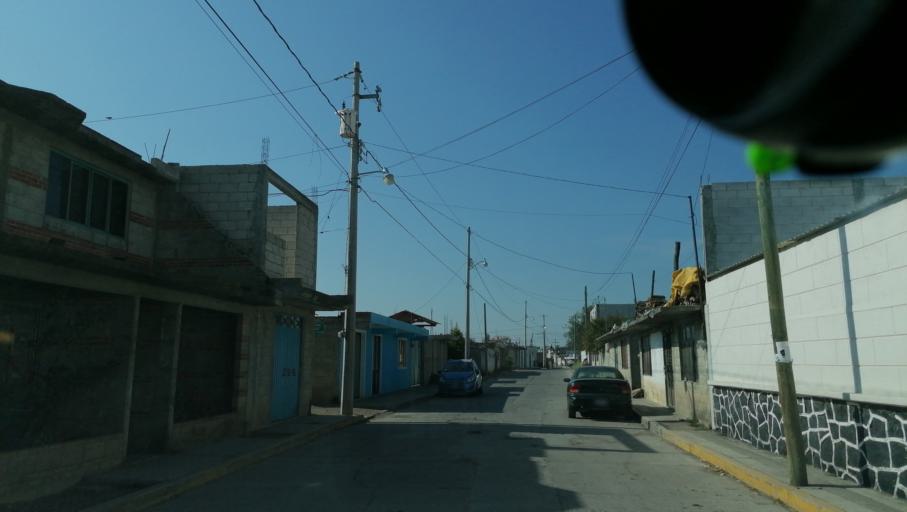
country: MX
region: Puebla
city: Domingo Arenas
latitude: 19.1420
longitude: -98.4534
